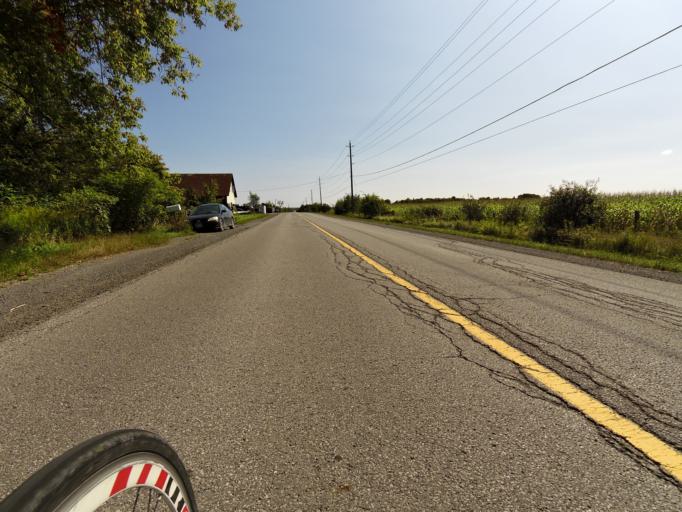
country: CA
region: Ontario
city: Arnprior
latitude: 45.4742
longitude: -76.1146
